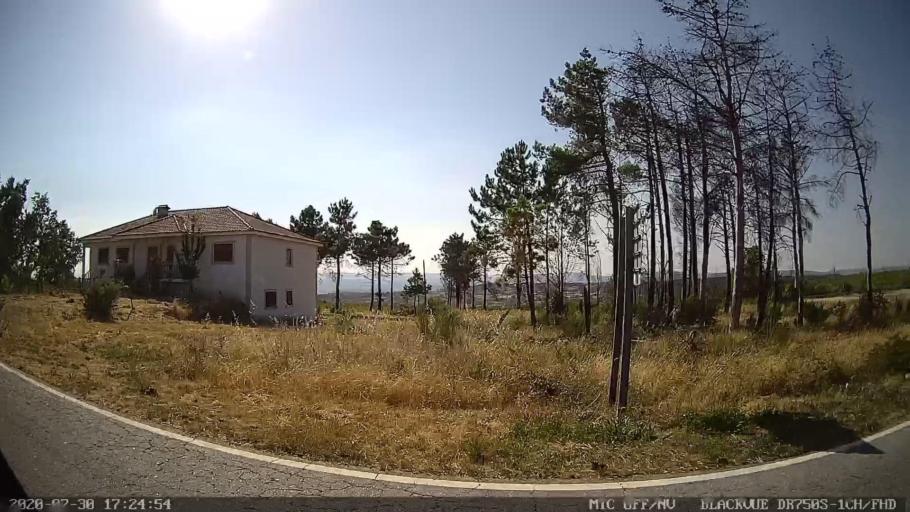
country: PT
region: Vila Real
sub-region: Murca
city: Murca
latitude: 41.3145
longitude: -7.4693
